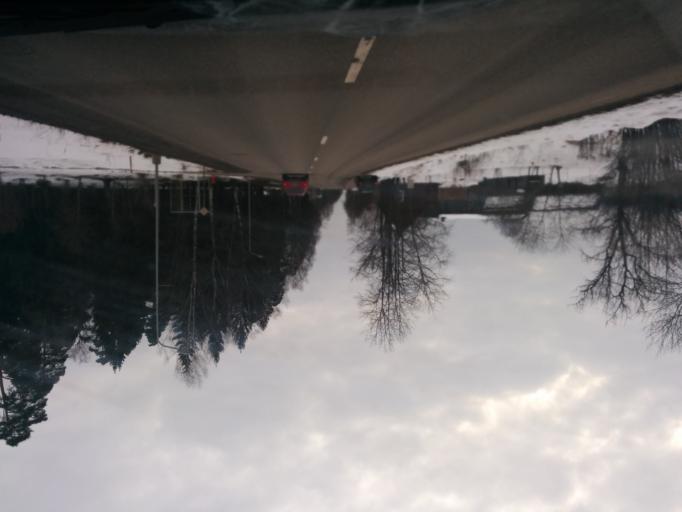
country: LV
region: Gulbenes Rajons
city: Gulbene
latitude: 57.1695
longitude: 26.7866
